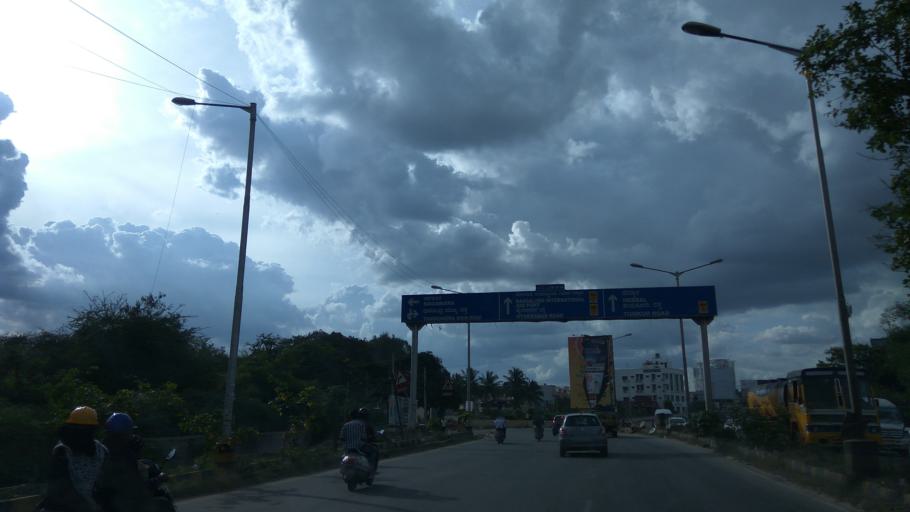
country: IN
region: Karnataka
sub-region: Bangalore Urban
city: Yelahanka
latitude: 13.0374
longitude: 77.6267
